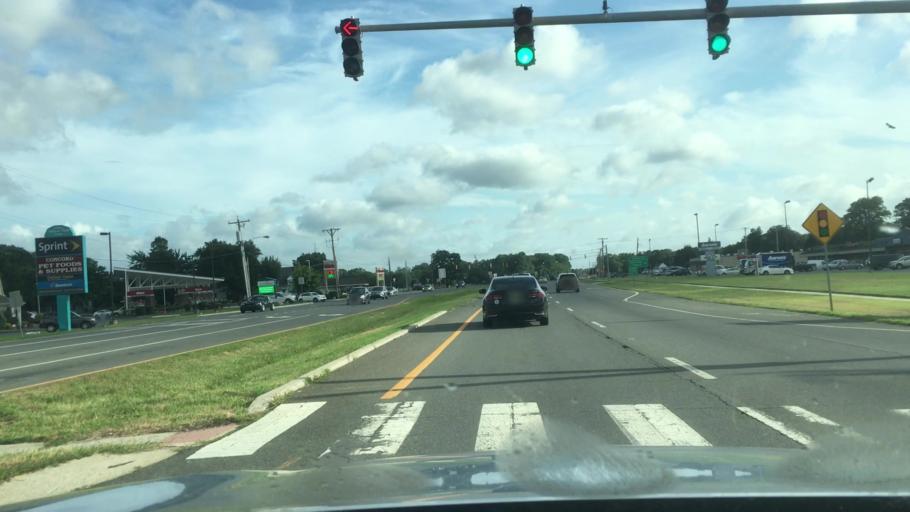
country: US
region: Delaware
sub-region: Sussex County
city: Milford
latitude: 38.9296
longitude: -75.4317
